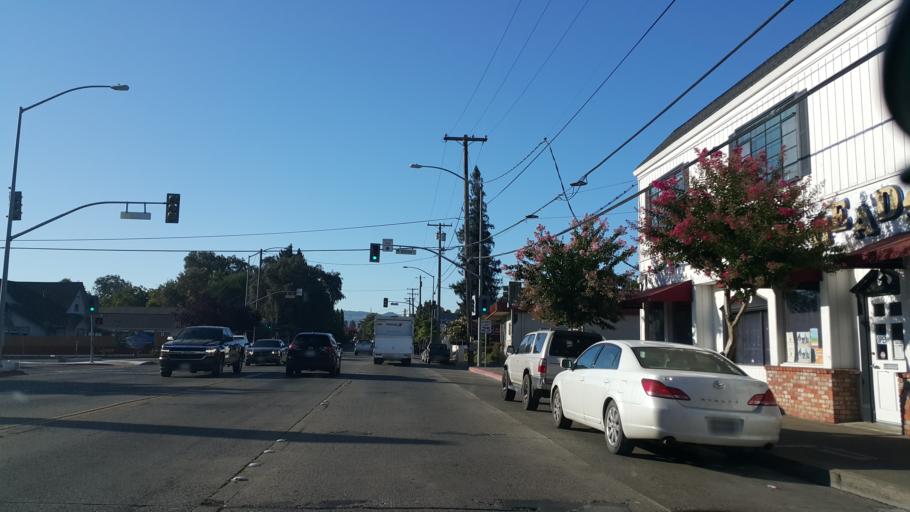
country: US
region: California
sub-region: Mendocino County
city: Ukiah
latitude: 39.1545
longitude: -123.2083
